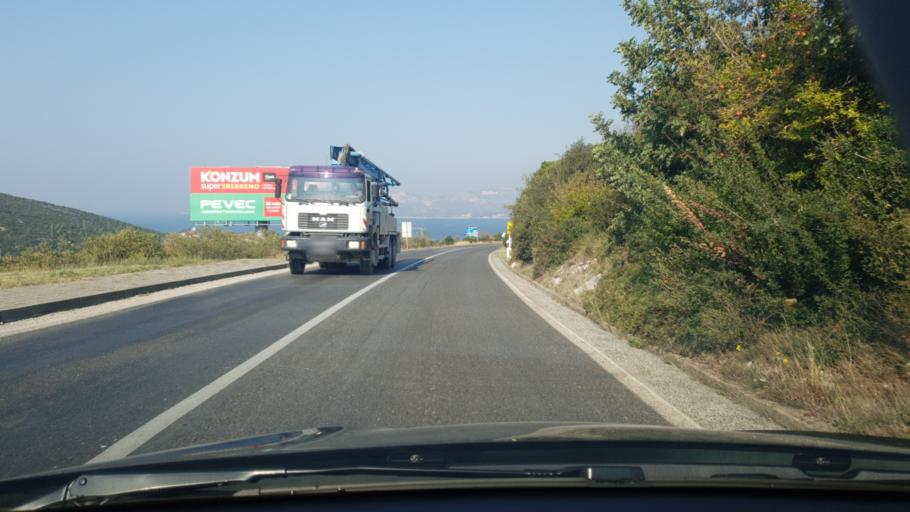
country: HR
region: Dubrovacko-Neretvanska
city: Cavtat
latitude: 42.5733
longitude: 18.2414
